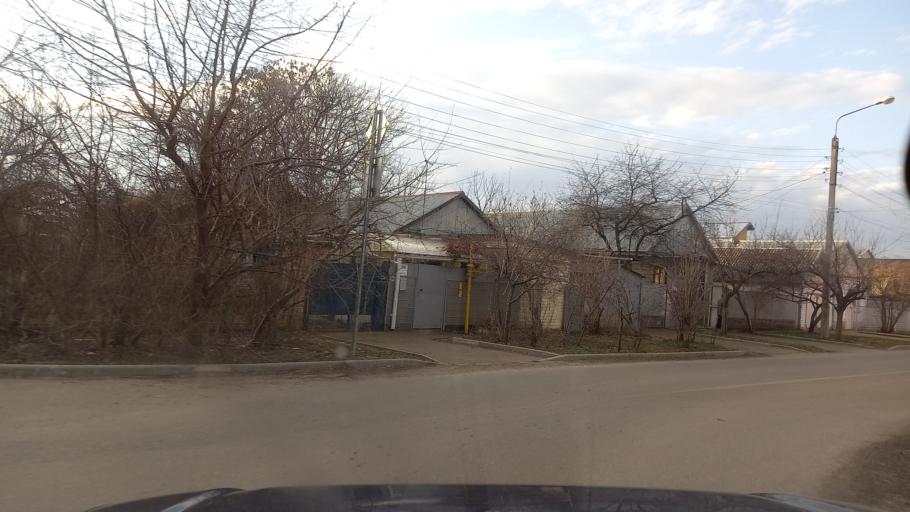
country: RU
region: Krasnodarskiy
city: Pashkovskiy
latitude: 45.0129
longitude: 39.1038
